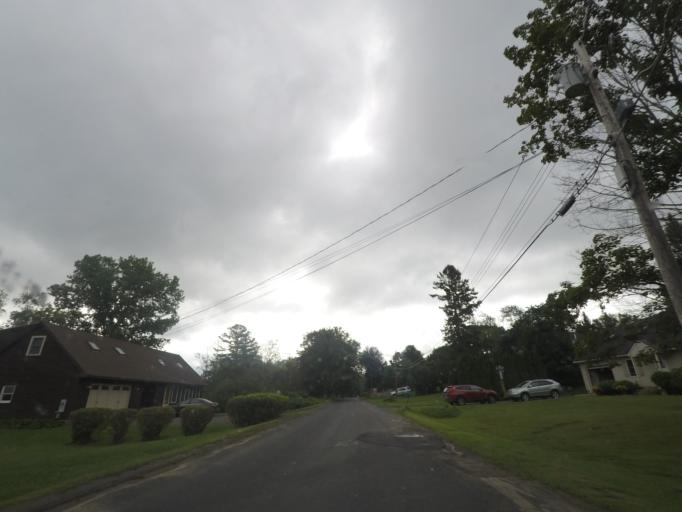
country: US
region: Massachusetts
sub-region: Berkshire County
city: Pittsfield
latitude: 42.4242
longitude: -73.3127
